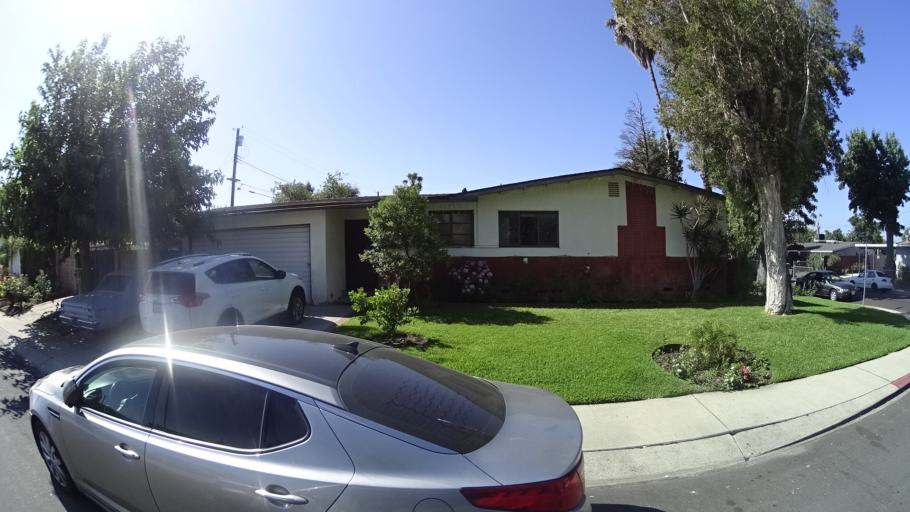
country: US
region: California
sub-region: Los Angeles County
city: Van Nuys
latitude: 34.2261
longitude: -118.4351
